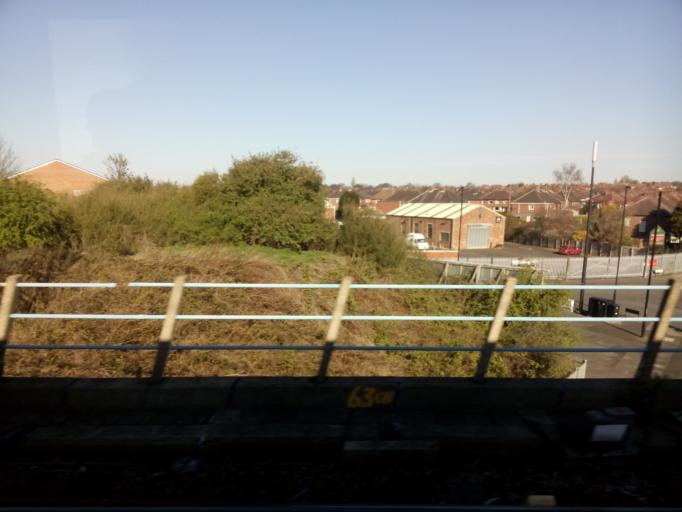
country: GB
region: England
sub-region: Borough of North Tyneside
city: Wallsend
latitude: 54.9912
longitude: -1.5633
